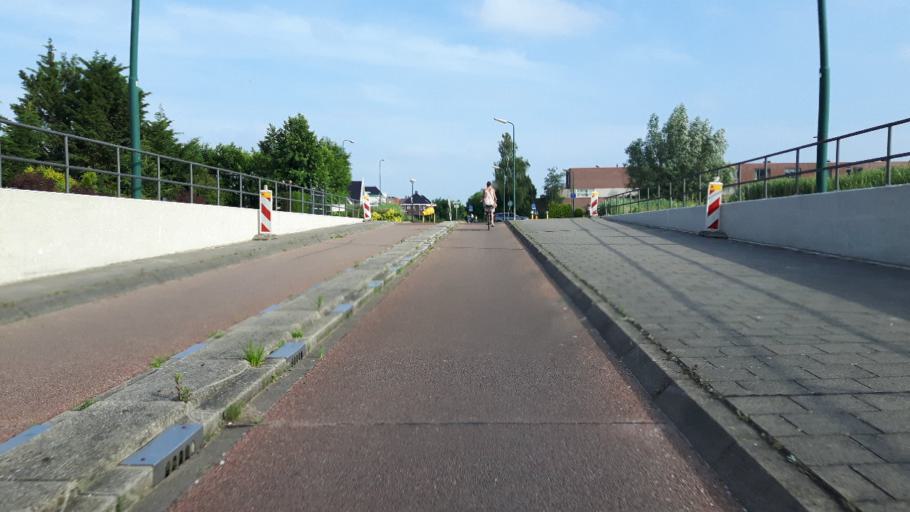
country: NL
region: Utrecht
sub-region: Gemeente Woerden
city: Woerden
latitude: 52.0885
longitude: 4.9062
